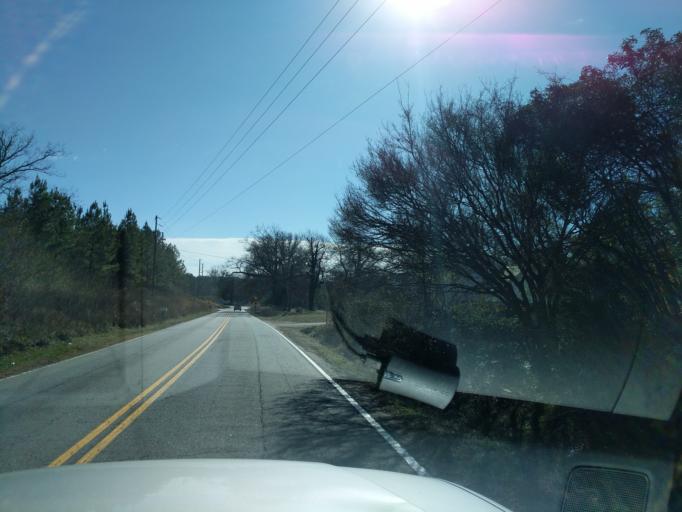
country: US
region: South Carolina
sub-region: Greenwood County
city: Ninety Six
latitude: 34.1820
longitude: -81.8683
